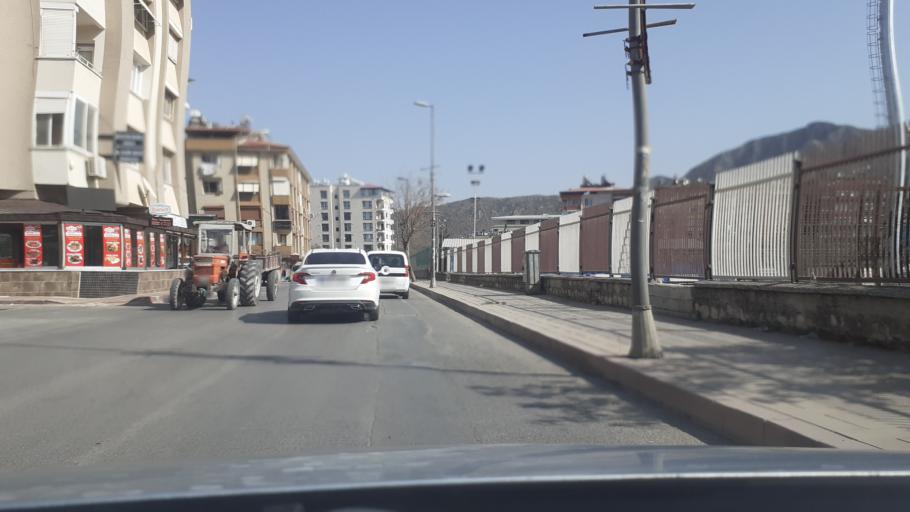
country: TR
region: Hatay
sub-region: Antakya Ilcesi
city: Antakya
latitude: 36.2127
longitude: 36.1581
